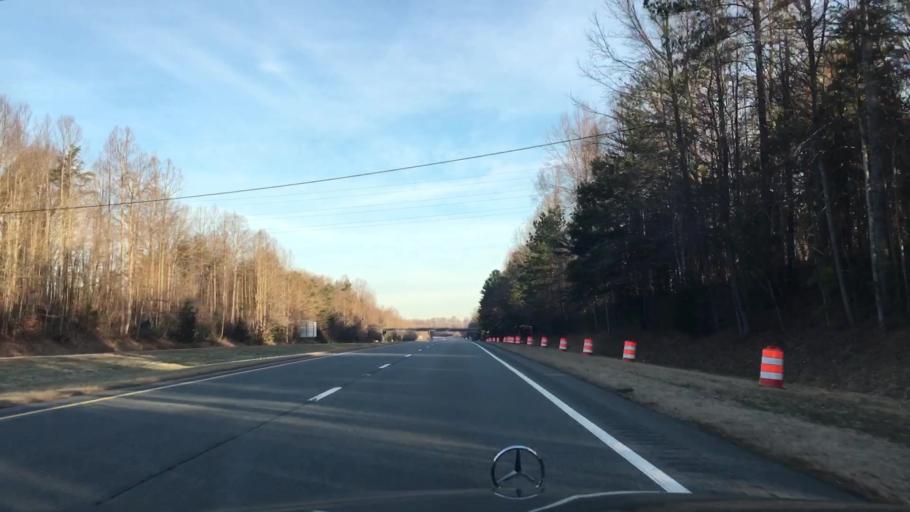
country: US
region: North Carolina
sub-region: Guilford County
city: Pleasant Garden
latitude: 36.0093
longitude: -79.7588
